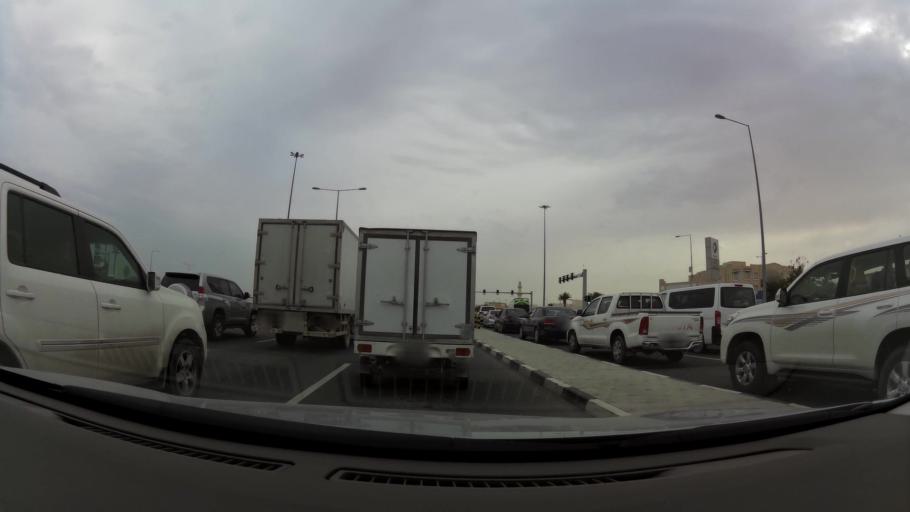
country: QA
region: Baladiyat ad Dawhah
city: Doha
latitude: 25.3230
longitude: 51.4864
